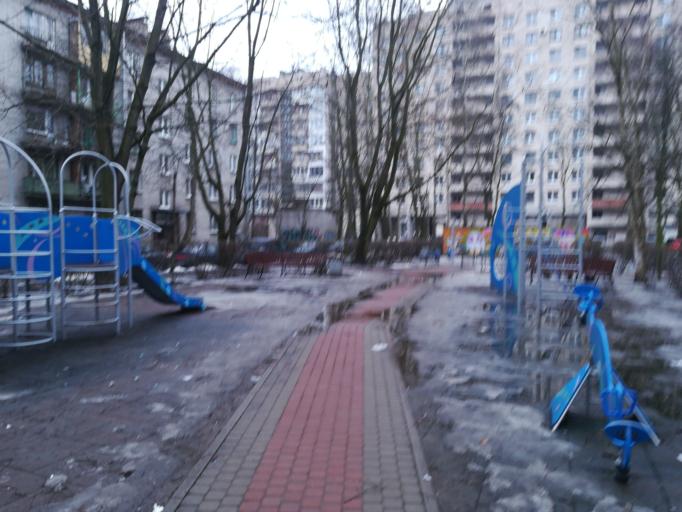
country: RU
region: St.-Petersburg
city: Vasyl'evsky Ostrov
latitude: 59.9500
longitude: 30.2426
